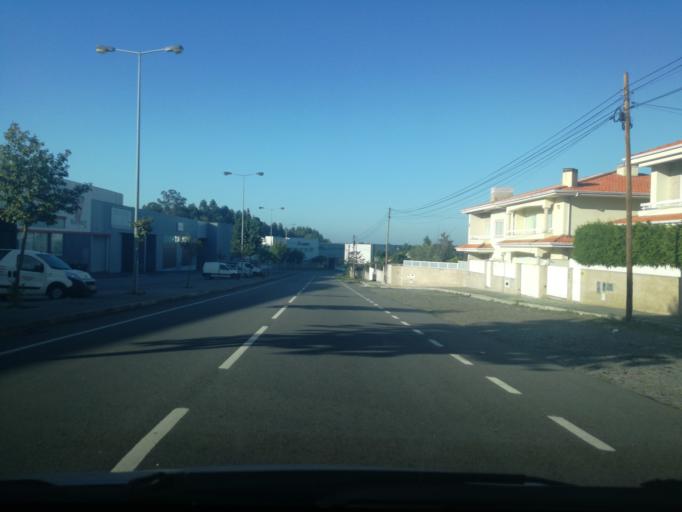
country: PT
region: Porto
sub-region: Maia
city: Milheiros
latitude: 41.2267
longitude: -8.5819
